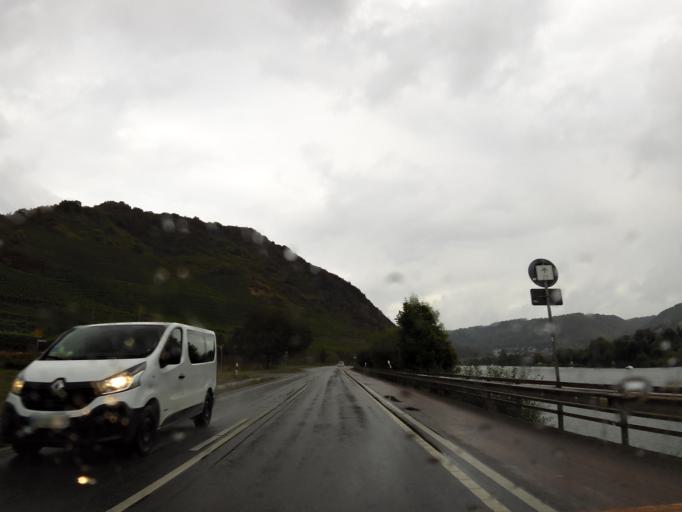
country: DE
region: Rheinland-Pfalz
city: Pommern
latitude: 50.1702
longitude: 7.2829
